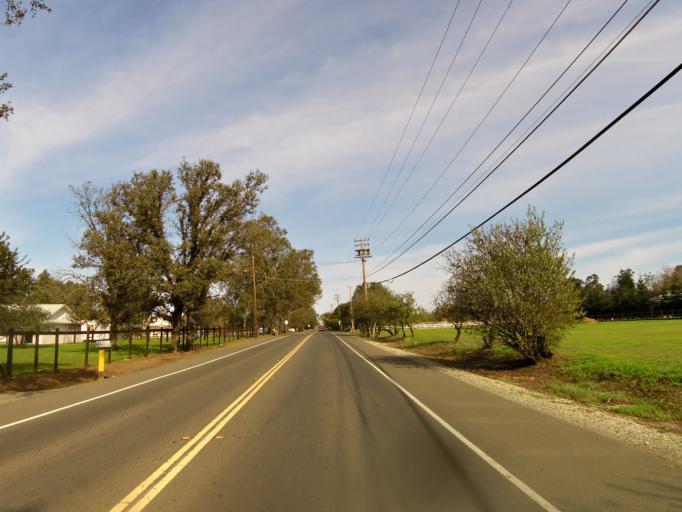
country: US
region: California
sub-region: Sacramento County
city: Wilton
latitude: 38.4371
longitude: -121.2938
